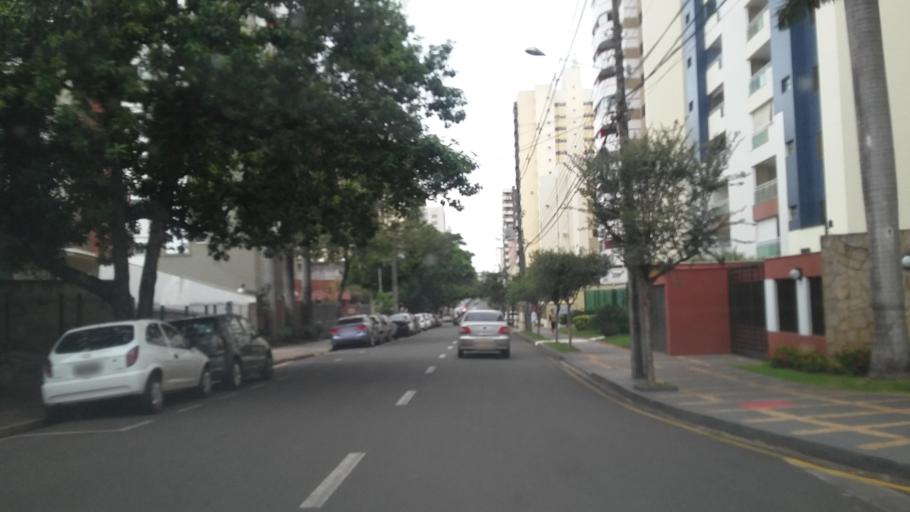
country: BR
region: Parana
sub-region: Londrina
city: Londrina
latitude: -23.3066
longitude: -51.1795
